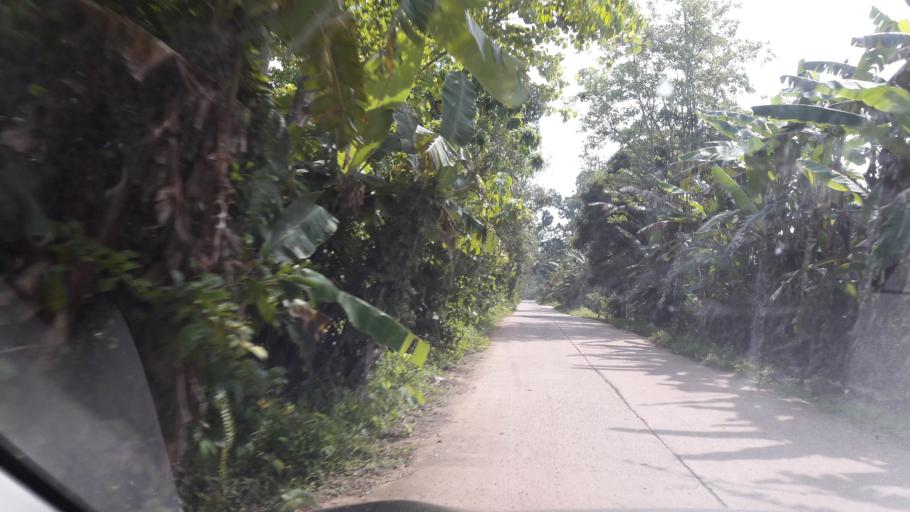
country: ID
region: South Sumatra
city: Prabumulih
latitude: -3.3237
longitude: 104.1135
